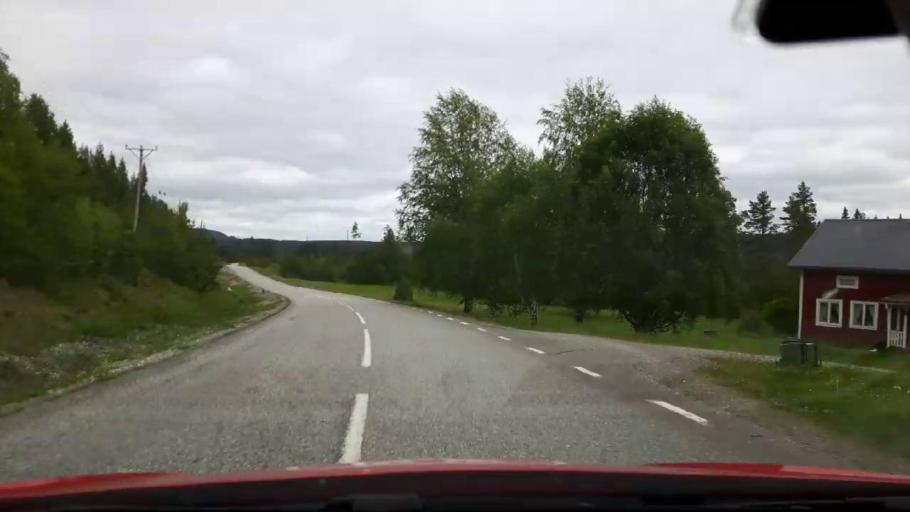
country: SE
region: Jaemtland
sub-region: Stroemsunds Kommun
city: Stroemsund
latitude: 63.2924
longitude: 15.7722
